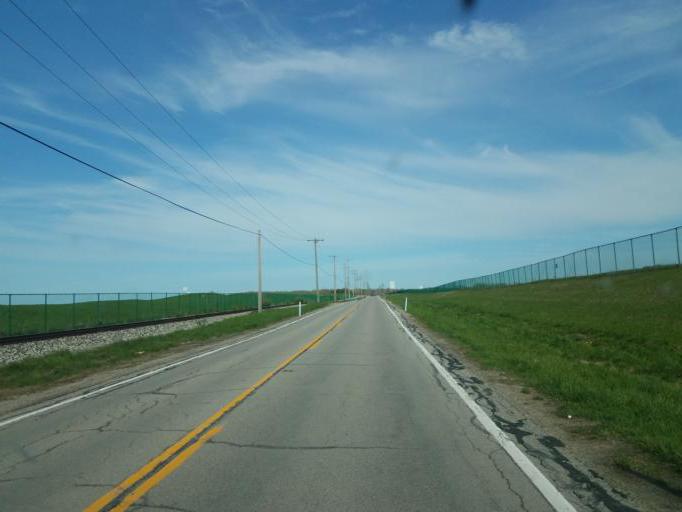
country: US
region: Ohio
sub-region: Lake County
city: Fairport Harbor
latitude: 41.7555
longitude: -81.2571
